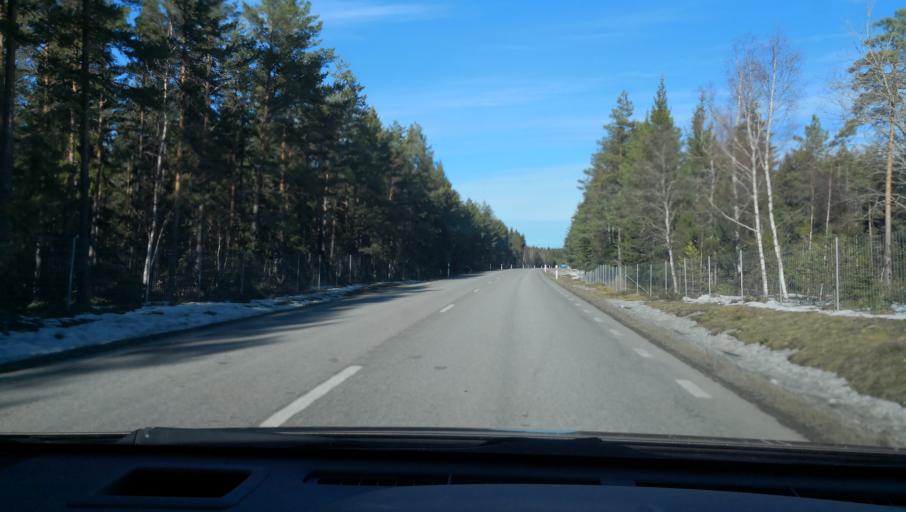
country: SE
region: Uppsala
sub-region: Uppsala Kommun
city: Vattholma
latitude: 60.0476
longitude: 17.7511
